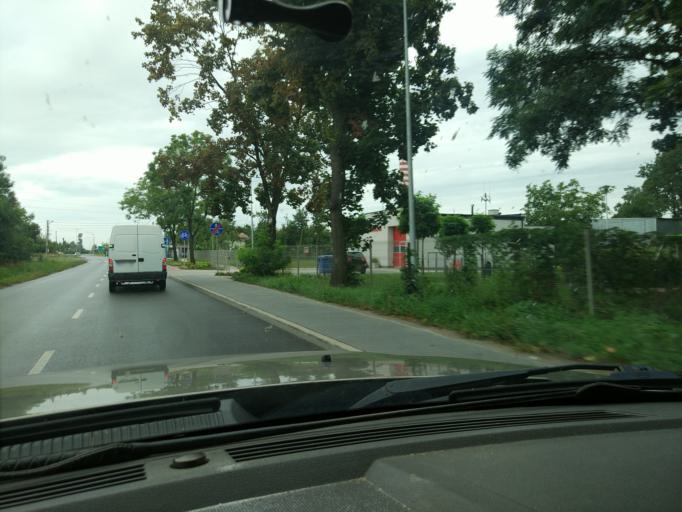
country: PL
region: Masovian Voivodeship
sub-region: Powiat pruszkowski
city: Brwinow
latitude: 52.1821
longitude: 20.7501
